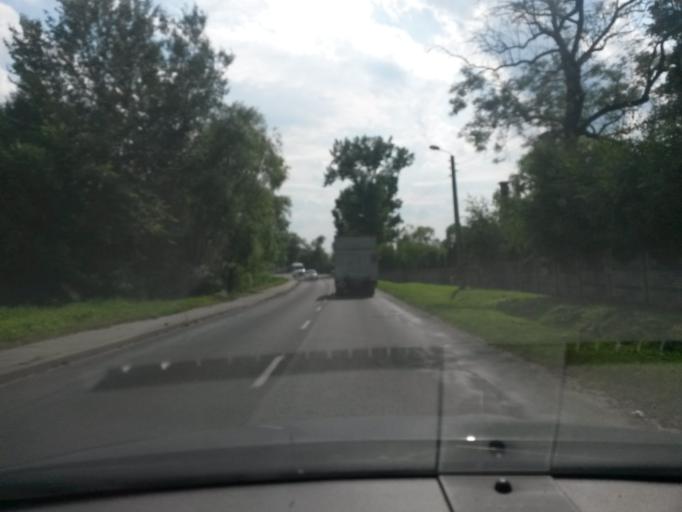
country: PL
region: Greater Poland Voivodeship
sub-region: Powiat poznanski
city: Kleszczewo
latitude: 52.3011
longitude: 17.1244
